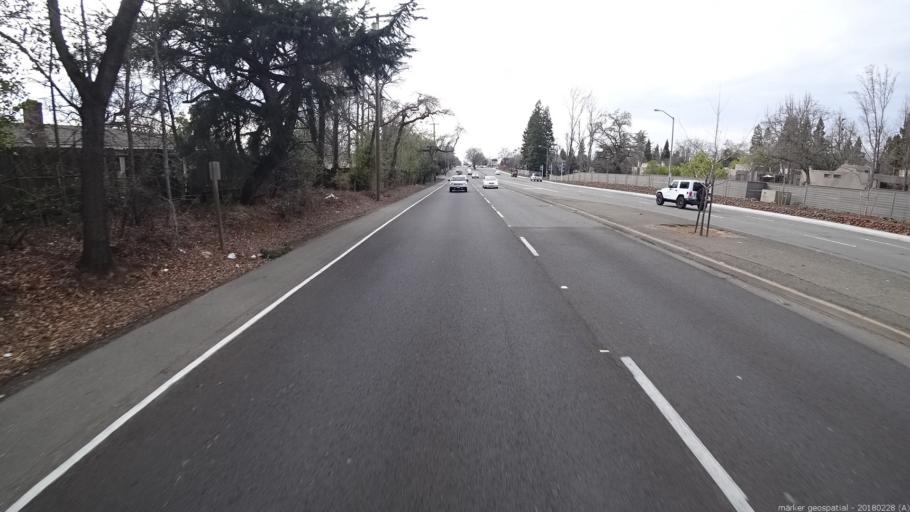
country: US
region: California
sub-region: Sacramento County
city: Fair Oaks
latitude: 38.6639
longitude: -121.2676
